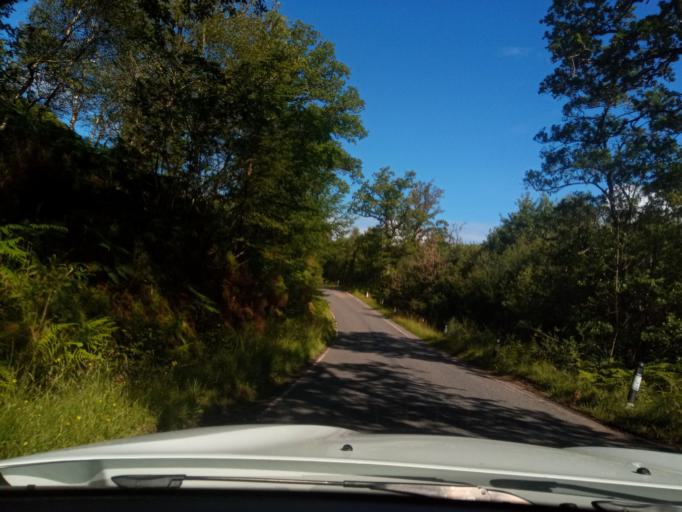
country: GB
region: Scotland
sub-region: Argyll and Bute
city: Isle Of Mull
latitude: 56.6970
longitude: -5.6855
